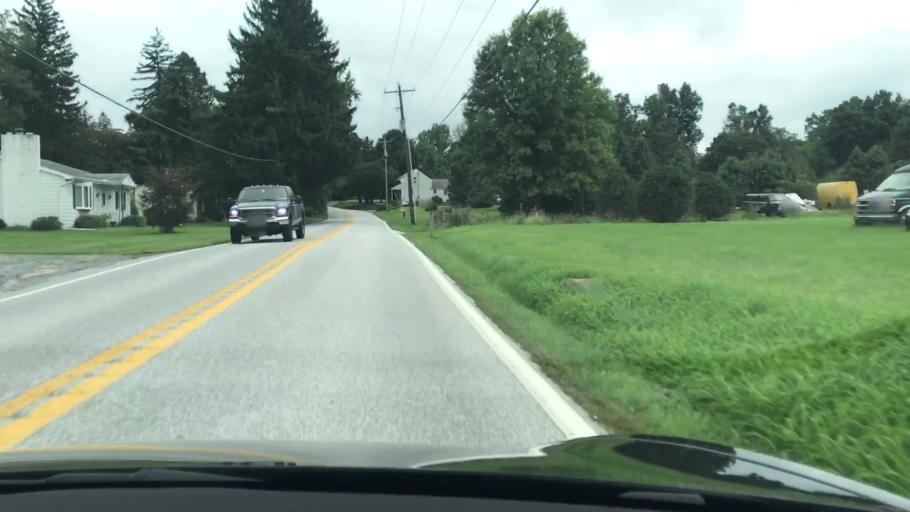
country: US
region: Pennsylvania
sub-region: York County
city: Dillsburg
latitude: 40.1403
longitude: -76.9644
